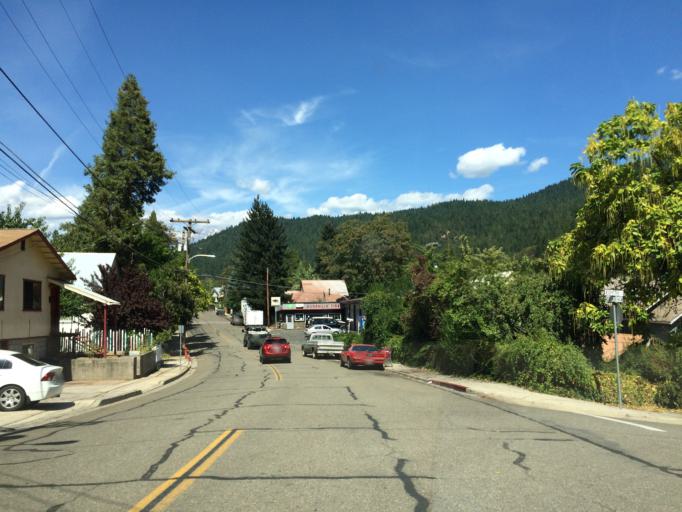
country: US
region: California
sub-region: Siskiyou County
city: Dunsmuir
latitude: 41.2045
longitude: -122.2744
